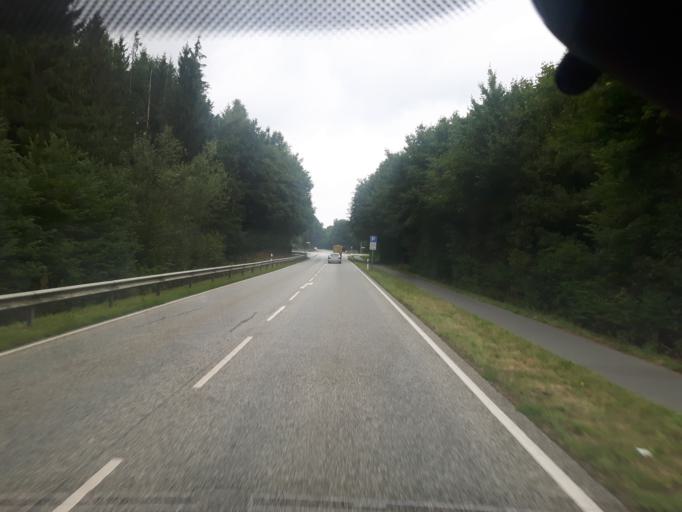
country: DE
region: Schleswig-Holstein
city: Borgstedt
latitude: 54.3564
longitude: 9.7041
